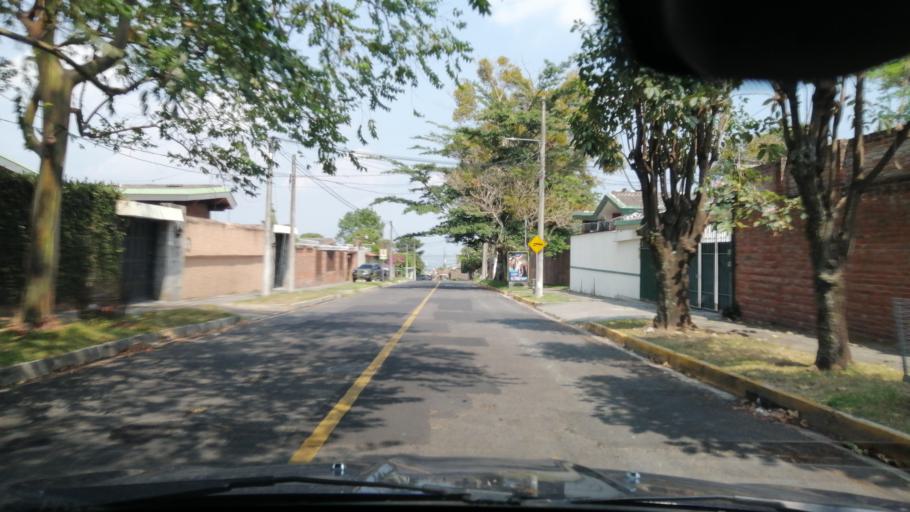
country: SV
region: La Libertad
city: Antiguo Cuscatlan
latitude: 13.6982
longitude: -89.2468
